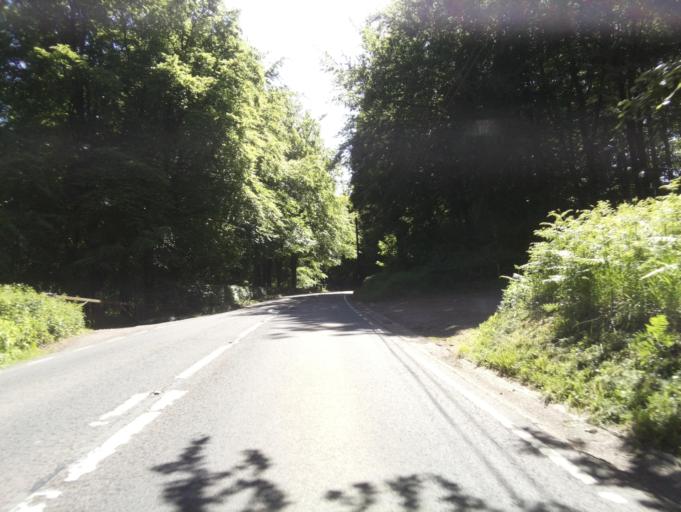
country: GB
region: England
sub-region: Devon
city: Honiton
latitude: 50.8657
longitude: -3.0897
